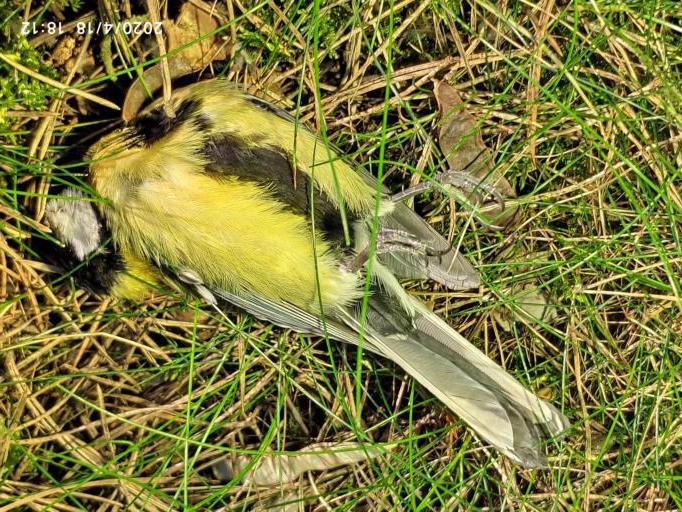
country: PL
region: Lubusz
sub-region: Powiat zielonogorski
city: Trzebiechow
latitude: 52.0961
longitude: 15.7054
